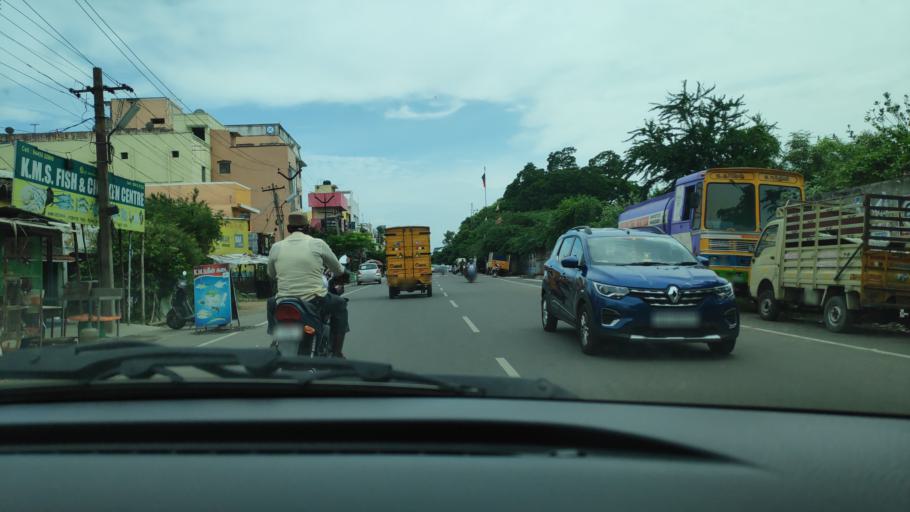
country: IN
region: Tamil Nadu
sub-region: Kancheepuram
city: Pallavaram
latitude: 12.9281
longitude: 80.1270
